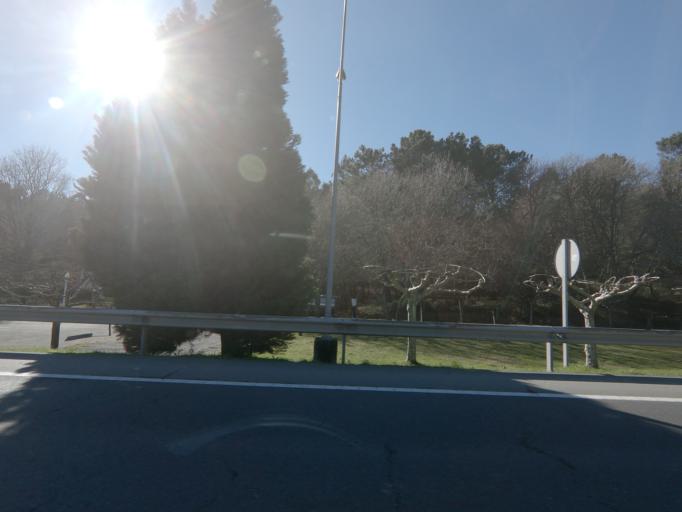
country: ES
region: Galicia
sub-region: Provincia de Pontevedra
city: Silleda
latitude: 42.6881
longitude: -8.2202
